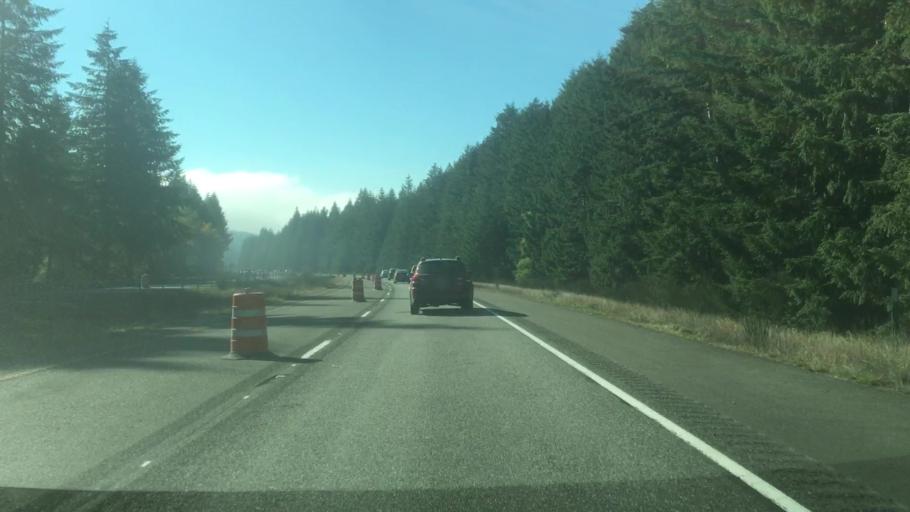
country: US
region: Washington
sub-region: Grays Harbor County
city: McCleary
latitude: 47.0485
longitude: -123.3079
